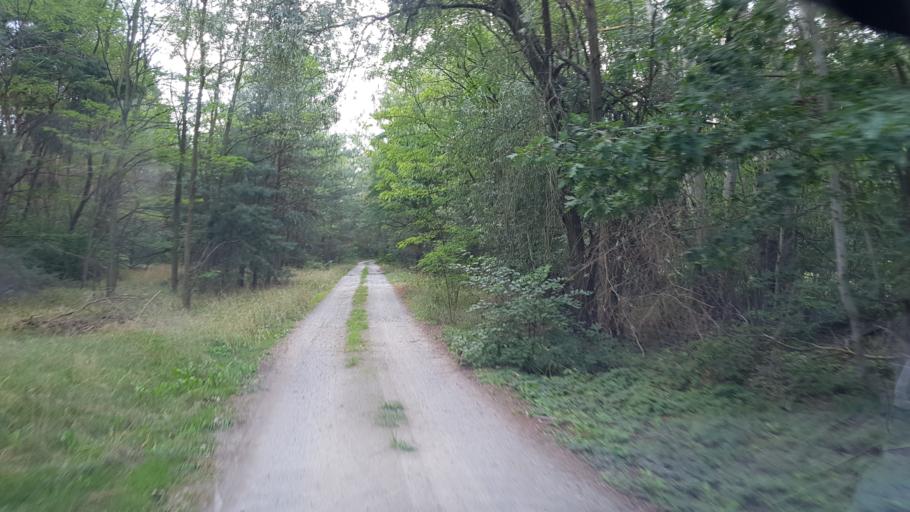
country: DE
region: Brandenburg
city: Lubbenau
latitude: 51.8043
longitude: 13.8887
